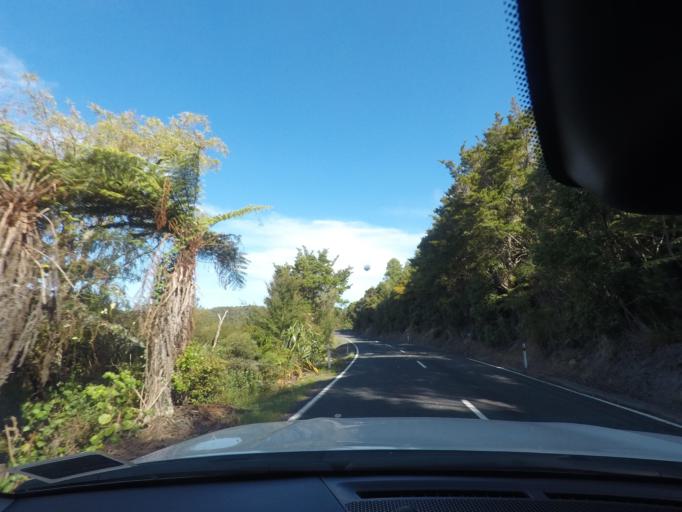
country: NZ
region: Northland
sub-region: Whangarei
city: Ngunguru
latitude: -35.6647
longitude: 174.4836
